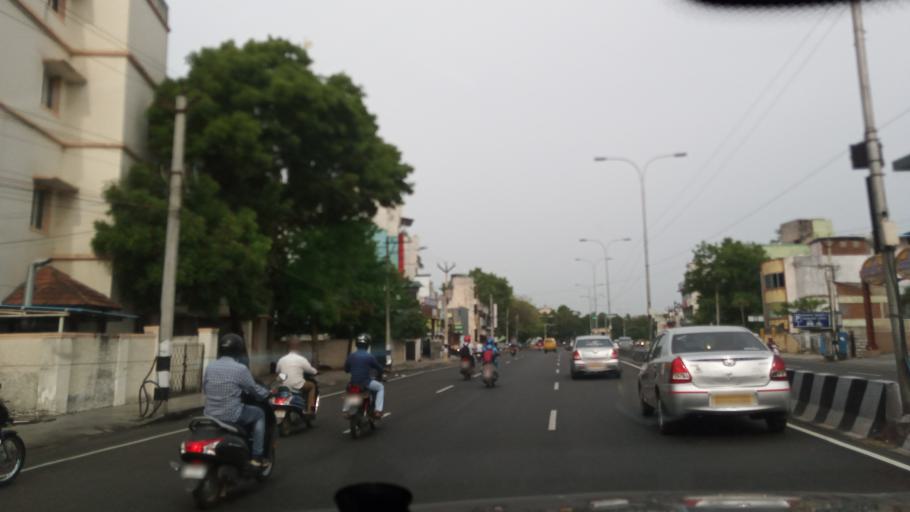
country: IN
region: Tamil Nadu
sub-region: Kancheepuram
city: Saint Thomas Mount
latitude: 13.0153
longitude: 80.1920
